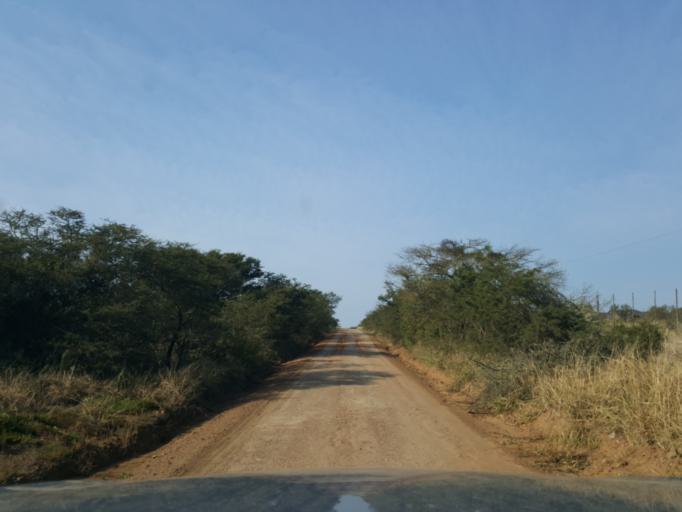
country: ZA
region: Eastern Cape
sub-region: Cacadu District Municipality
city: Grahamstown
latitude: -33.4069
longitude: 26.2978
